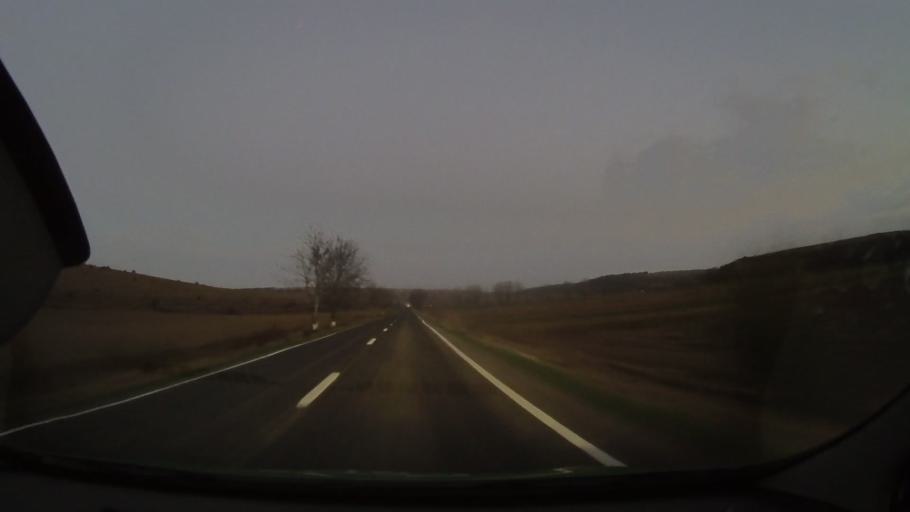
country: RO
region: Constanta
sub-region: Comuna Ion Corvin
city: Ion Corvin
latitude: 44.1033
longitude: 27.7882
